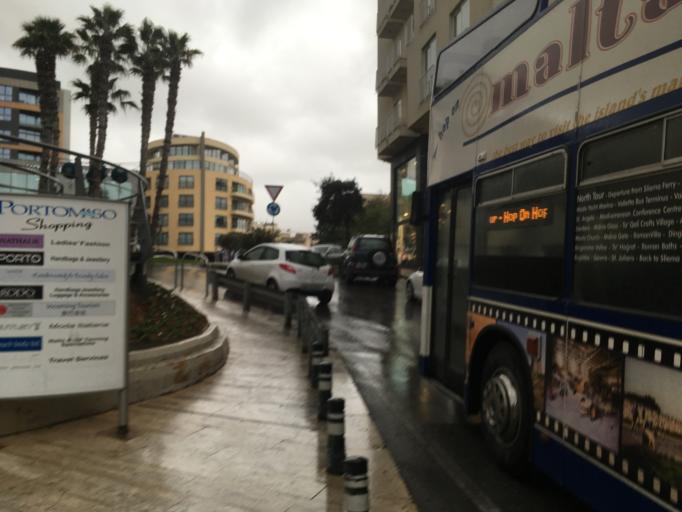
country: MT
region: Saint Julian
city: San Giljan
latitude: 35.9218
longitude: 14.4915
